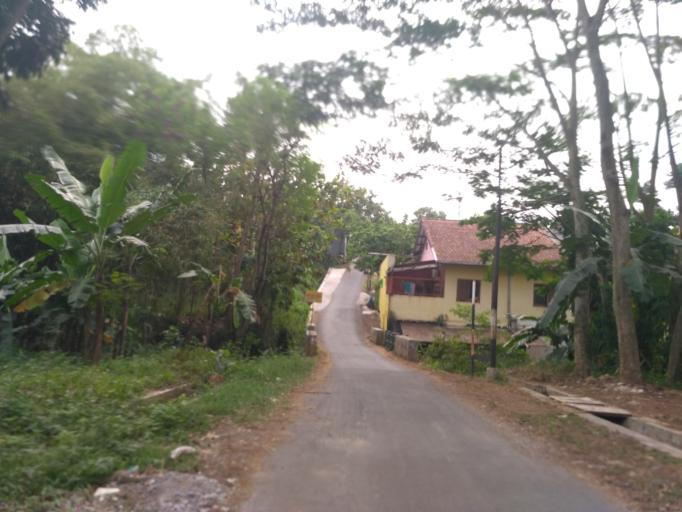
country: ID
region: Central Java
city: Ungaran
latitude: -7.0752
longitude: 110.4239
